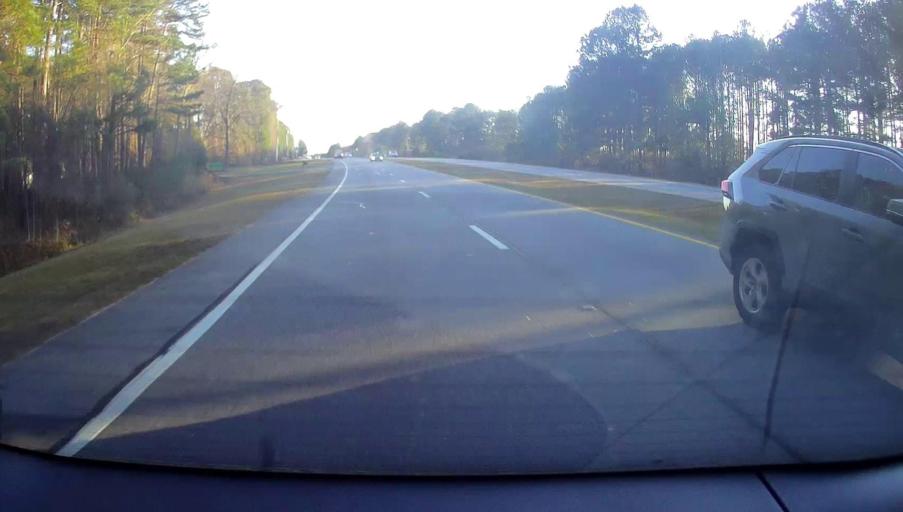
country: US
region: Georgia
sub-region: Fayette County
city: Peachtree City
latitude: 33.4219
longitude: -84.6038
